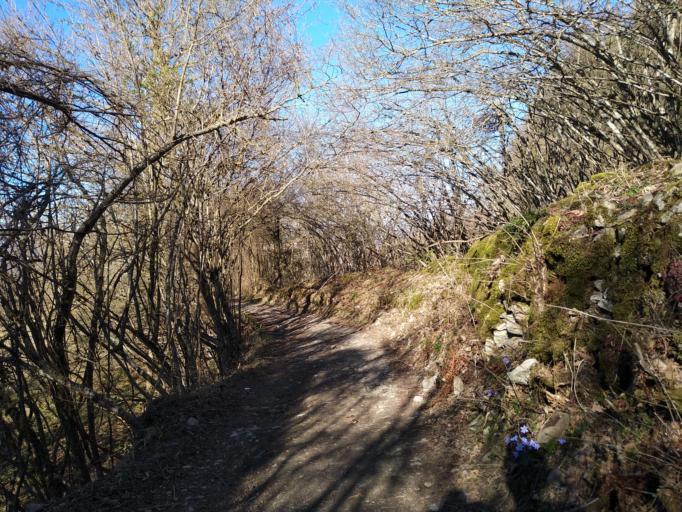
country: IT
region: Emilia-Romagna
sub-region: Provincia di Reggio Emilia
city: Castelnovo ne'Monti
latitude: 44.4251
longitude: 10.4134
